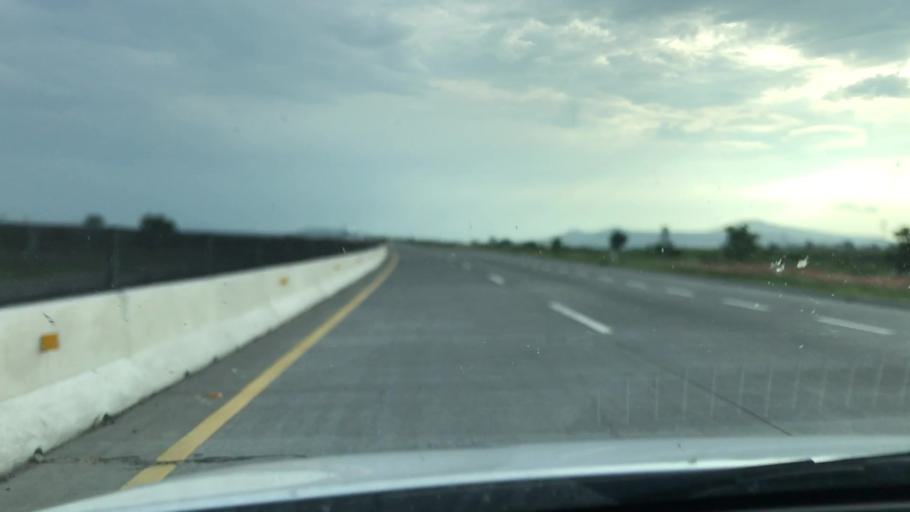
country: MX
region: Michoacan
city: La Piedad Cavadas
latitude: 20.3896
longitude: -102.1059
